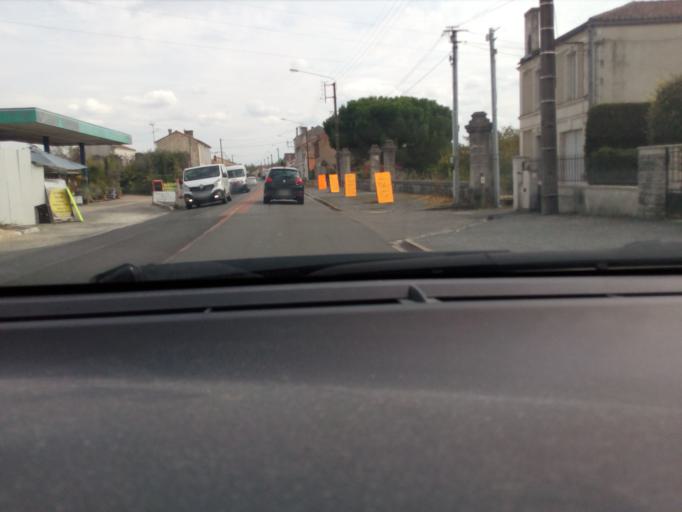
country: FR
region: Poitou-Charentes
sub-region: Departement de la Charente
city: Saint-Yrieix-sur-Charente
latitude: 45.6674
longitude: 0.1214
